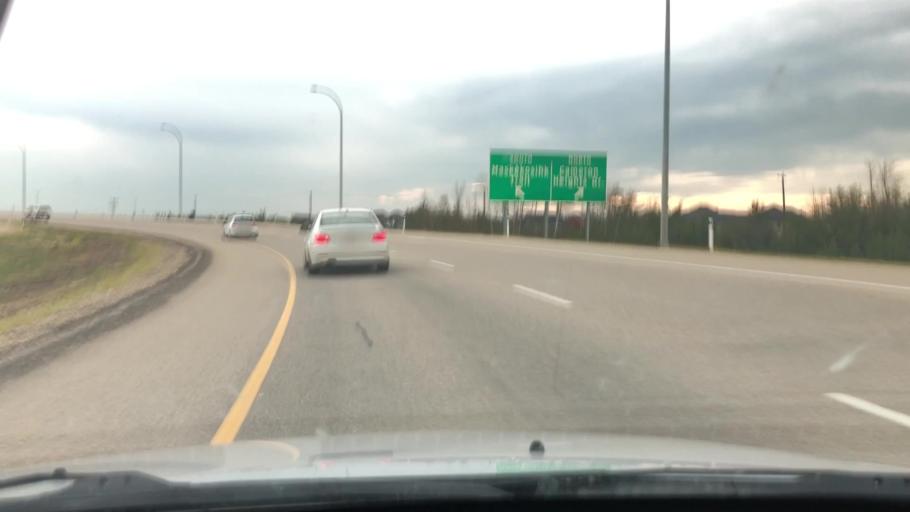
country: CA
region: Alberta
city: Devon
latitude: 53.4675
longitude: -113.6258
